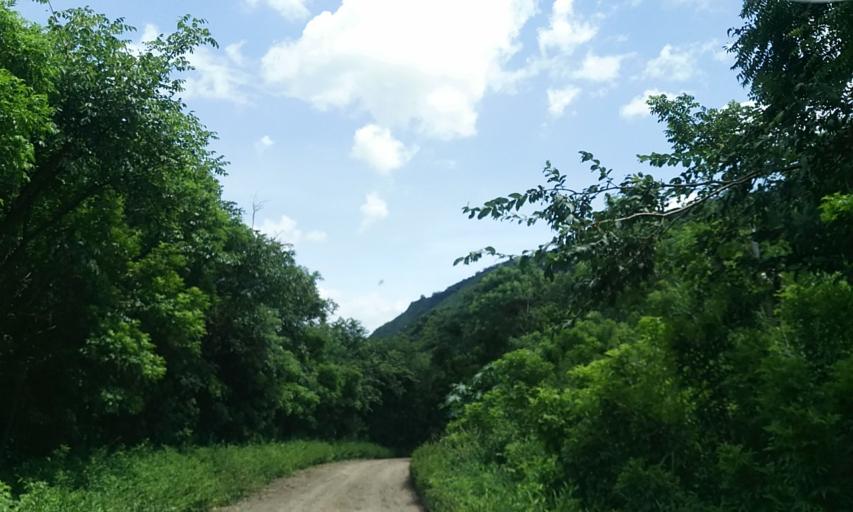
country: NI
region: Matagalpa
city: Terrabona
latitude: 12.7313
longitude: -85.9302
